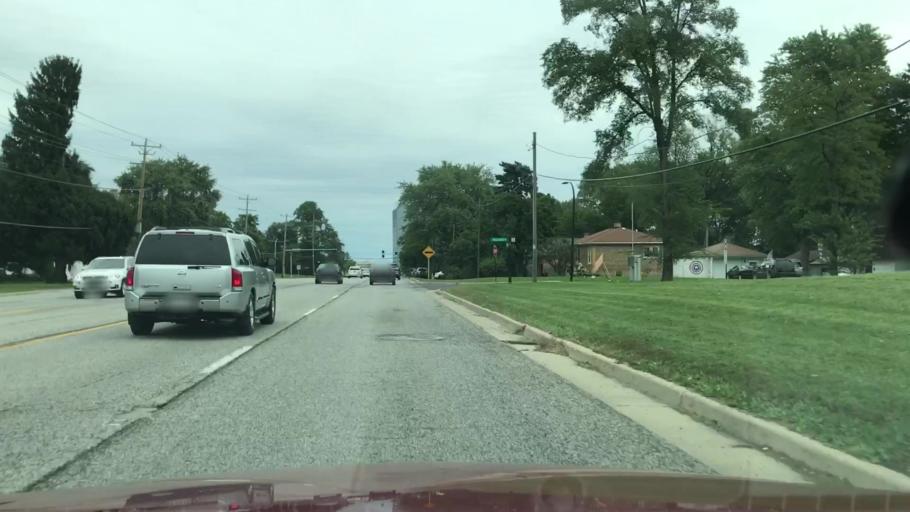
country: US
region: Illinois
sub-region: DuPage County
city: Oakbrook Terrace
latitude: 41.8521
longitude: -87.9703
